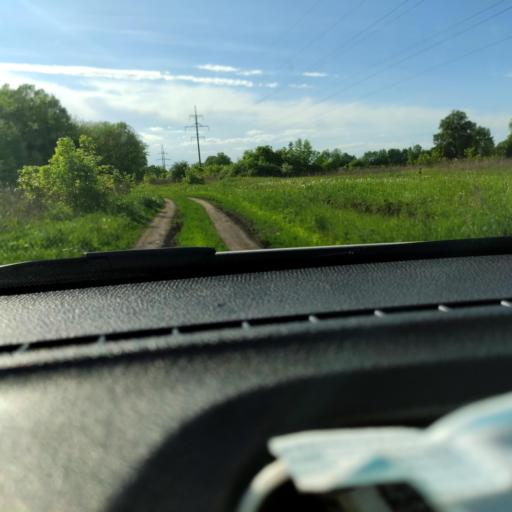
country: RU
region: Voronezj
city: Ramon'
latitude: 51.9468
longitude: 39.3650
